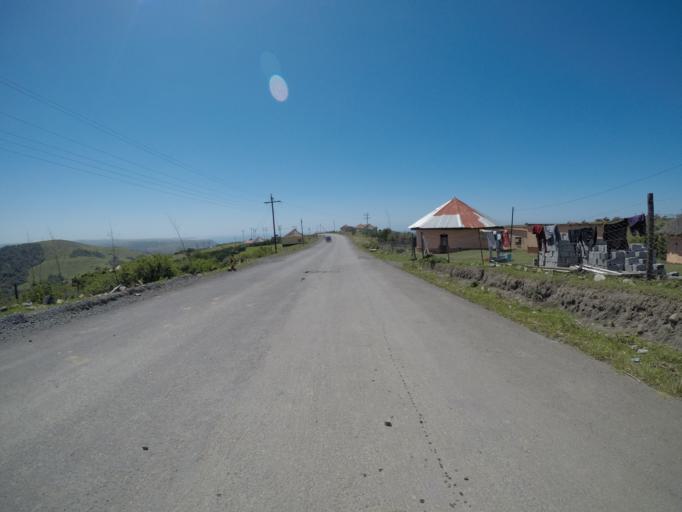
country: ZA
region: Eastern Cape
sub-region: OR Tambo District Municipality
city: Libode
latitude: -31.9969
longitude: 29.1247
